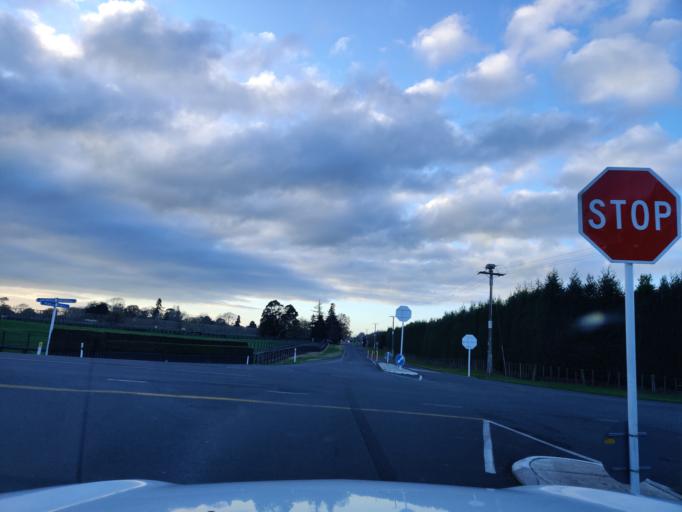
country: NZ
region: Waikato
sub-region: Waipa District
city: Cambridge
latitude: -37.8603
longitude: 175.4390
